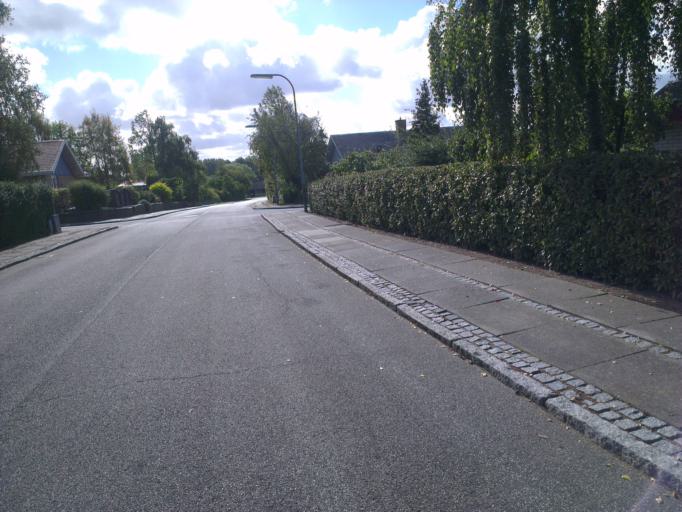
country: DK
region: Capital Region
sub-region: Frederikssund Kommune
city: Slangerup
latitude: 55.8520
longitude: 12.1665
